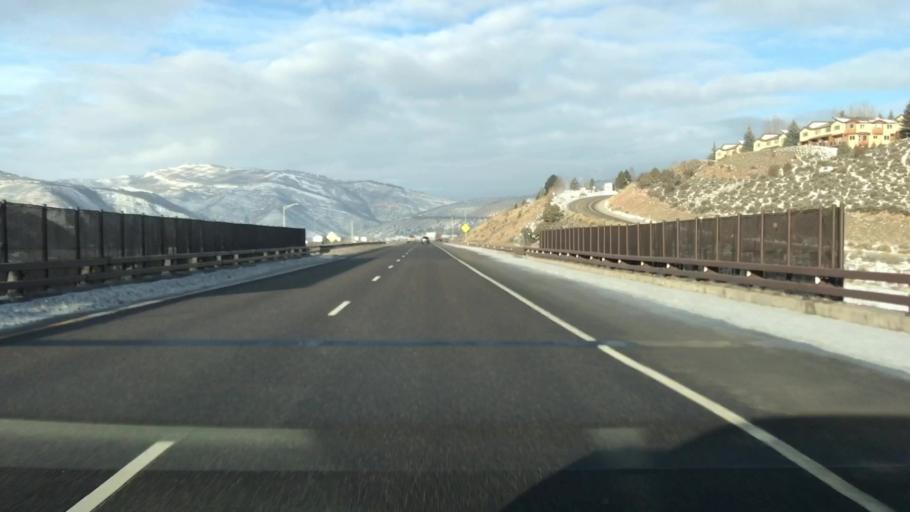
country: US
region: Colorado
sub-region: Eagle County
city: Edwards
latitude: 39.6497
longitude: -106.5877
